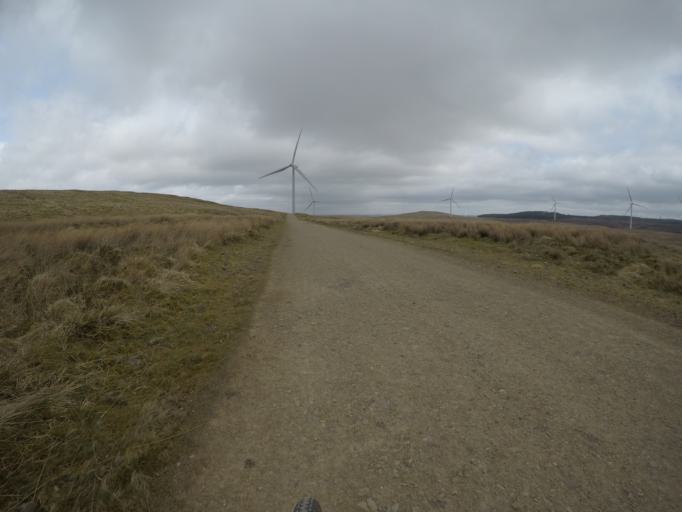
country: GB
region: Scotland
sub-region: East Renfrewshire
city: Eaglesham
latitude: 55.7047
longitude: -4.3168
